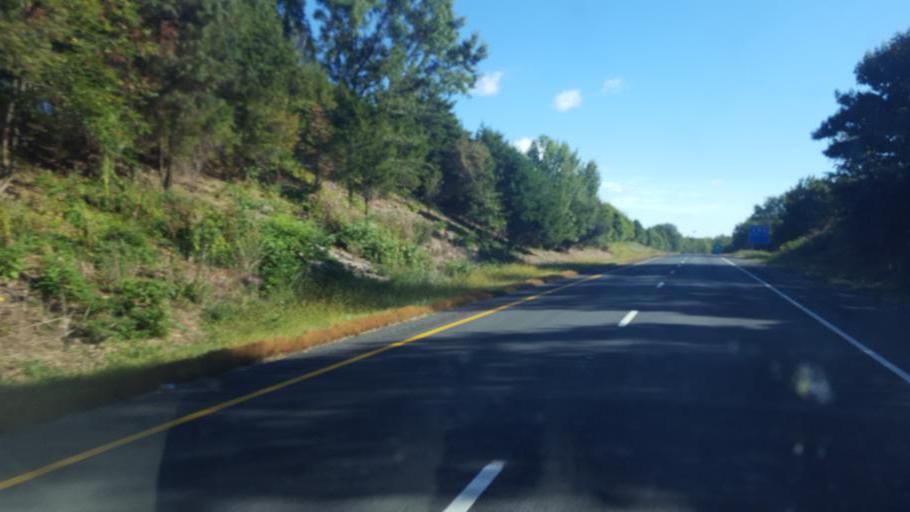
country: US
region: Maryland
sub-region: Washington County
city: Wilson-Conococheague
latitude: 39.6410
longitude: -77.9479
